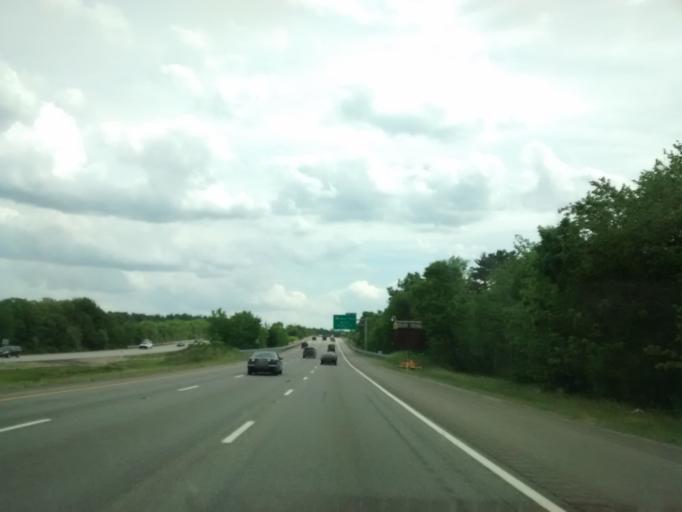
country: US
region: Massachusetts
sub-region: Worcester County
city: Cordaville
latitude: 42.2726
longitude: -71.5658
